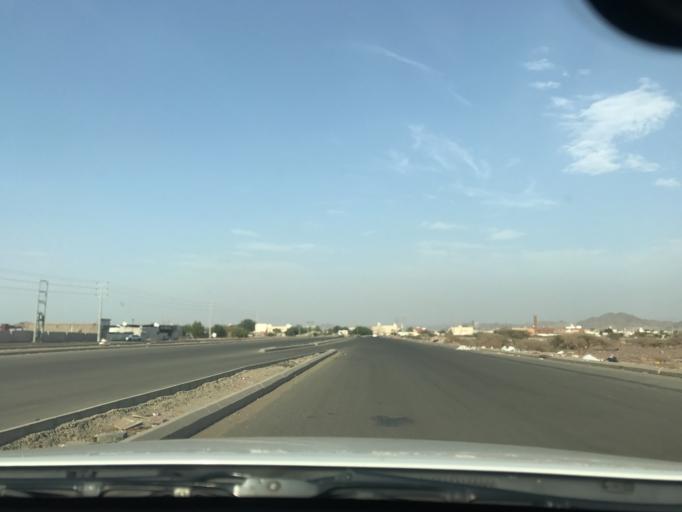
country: SA
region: Makkah
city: Al Jumum
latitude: 21.4539
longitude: 39.5431
